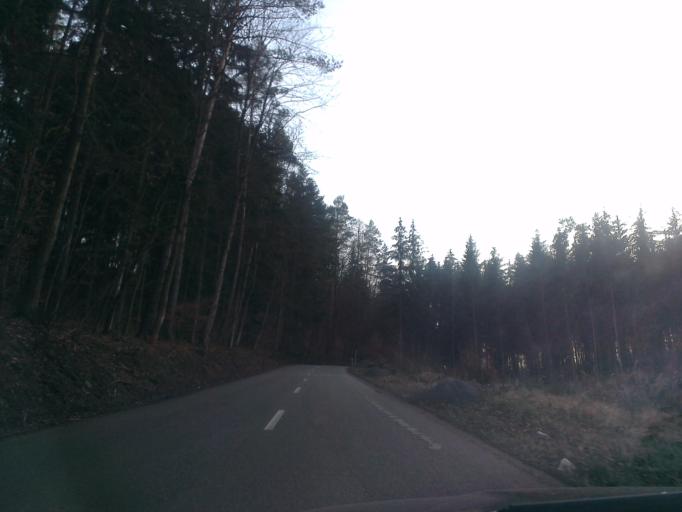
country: CZ
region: South Moravian
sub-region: Okres Blansko
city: Jedovnice
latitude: 49.2920
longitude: 16.7487
